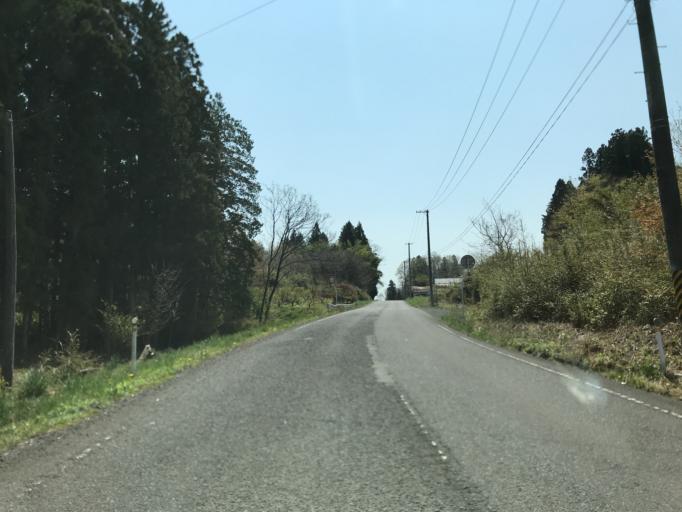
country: JP
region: Fukushima
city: Ishikawa
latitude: 37.1012
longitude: 140.4058
